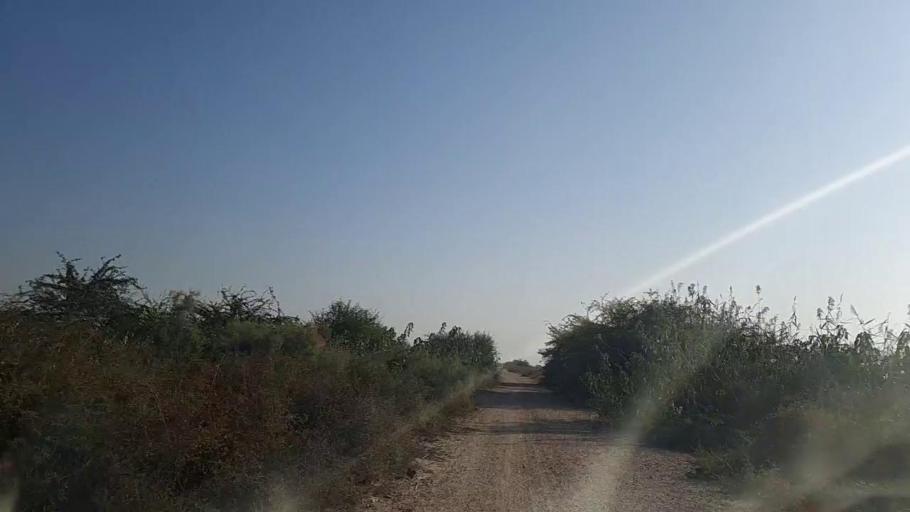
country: PK
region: Sindh
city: Jati
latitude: 24.3977
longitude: 68.2301
